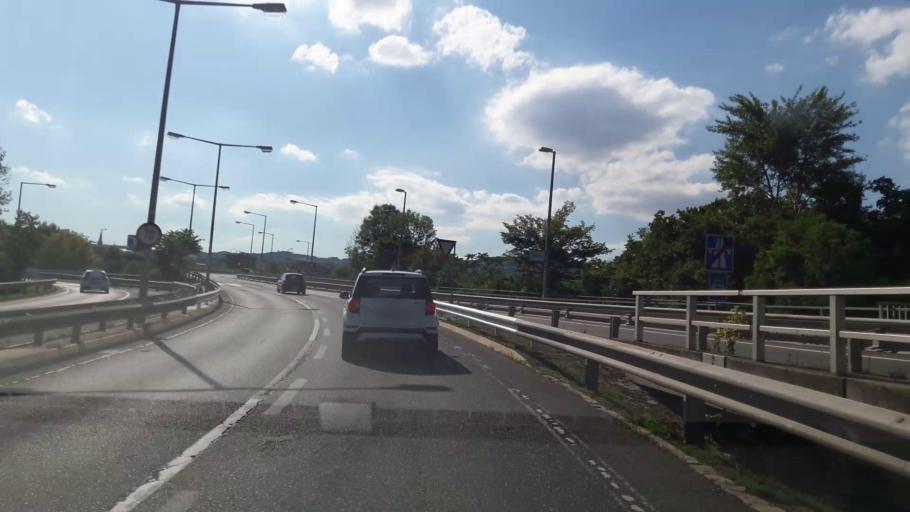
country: AT
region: Vienna
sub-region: Wien Stadt
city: Vienna
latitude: 48.2545
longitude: 16.3727
